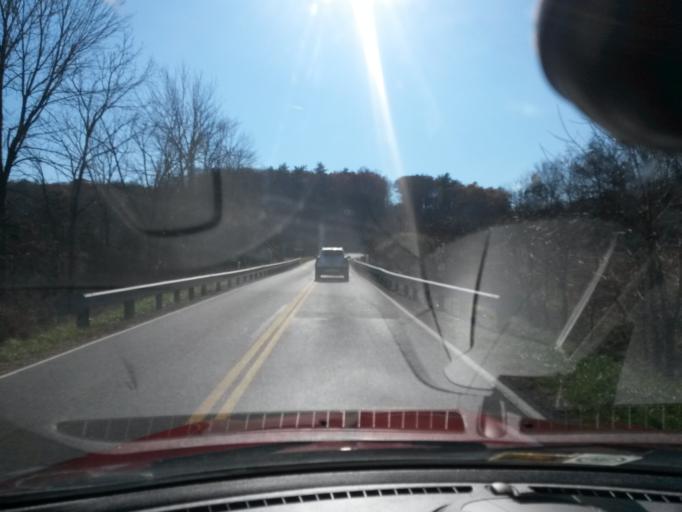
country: US
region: Virginia
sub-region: City of Bedford
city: Bedford
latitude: 37.3876
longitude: -79.5508
